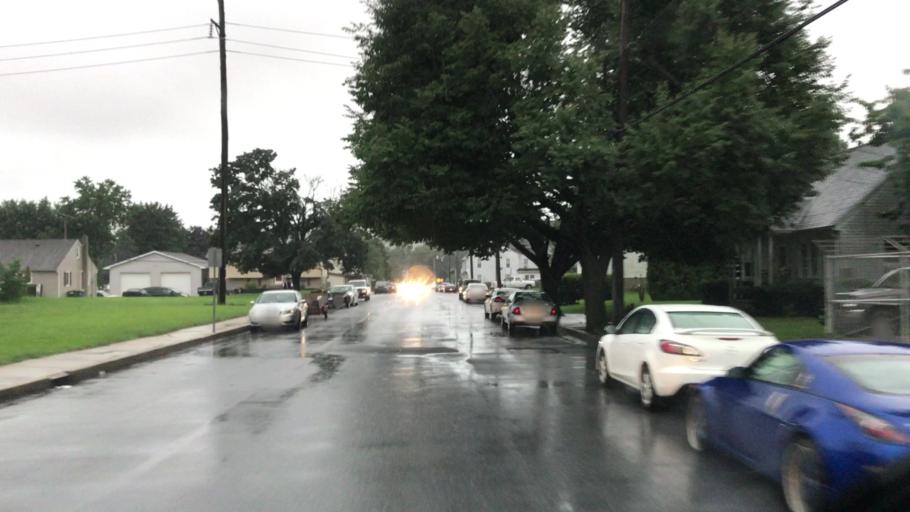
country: US
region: Pennsylvania
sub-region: Dauphin County
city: Middletown
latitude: 40.1908
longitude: -76.7370
